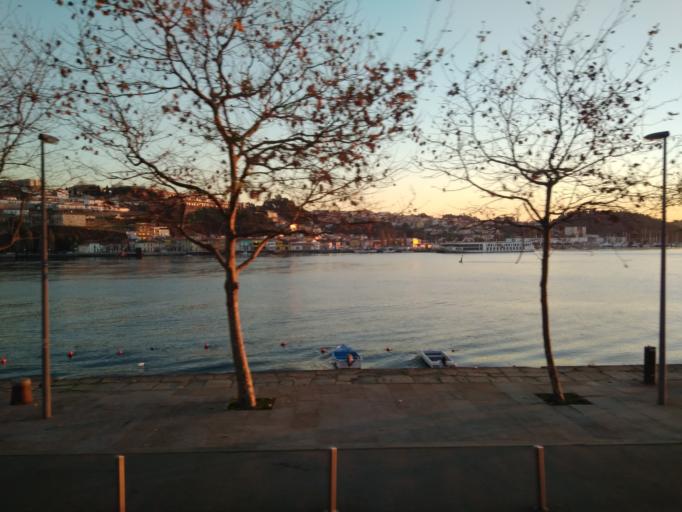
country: PT
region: Porto
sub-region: Vila Nova de Gaia
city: Canidelo
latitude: 41.1484
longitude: -8.6475
